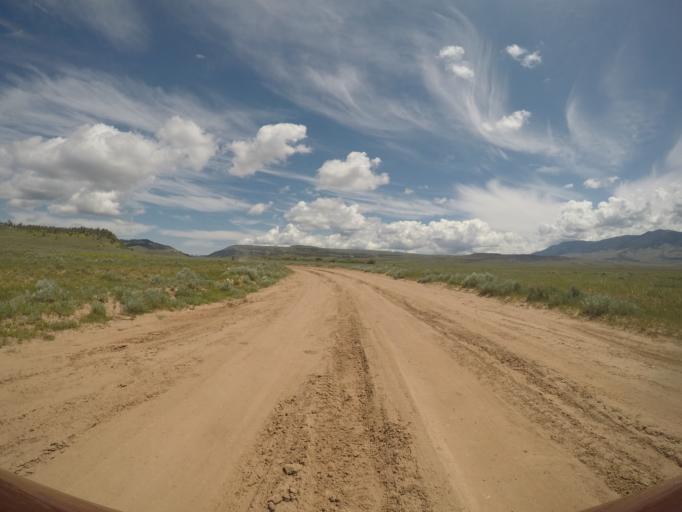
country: US
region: Montana
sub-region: Yellowstone County
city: Laurel
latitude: 45.2371
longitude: -108.6783
